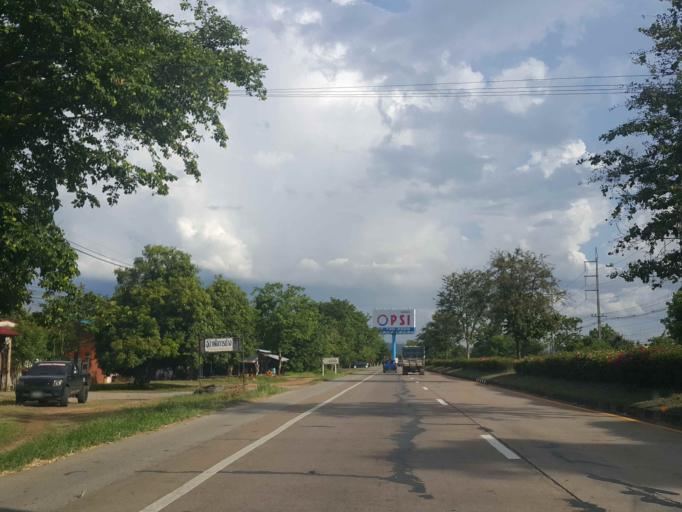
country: TH
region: Phrae
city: Sung Men
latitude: 18.0273
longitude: 100.1111
